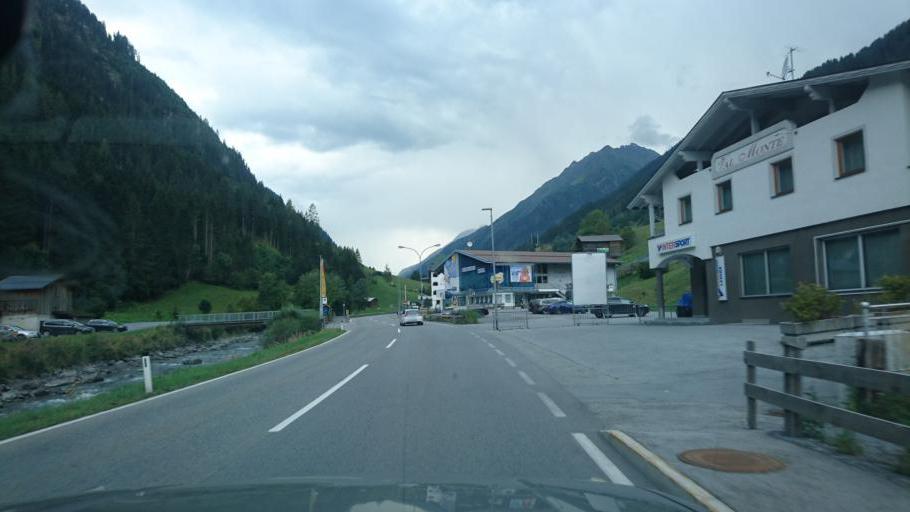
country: AT
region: Tyrol
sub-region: Politischer Bezirk Landeck
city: Kappl
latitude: 47.0609
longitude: 10.3756
